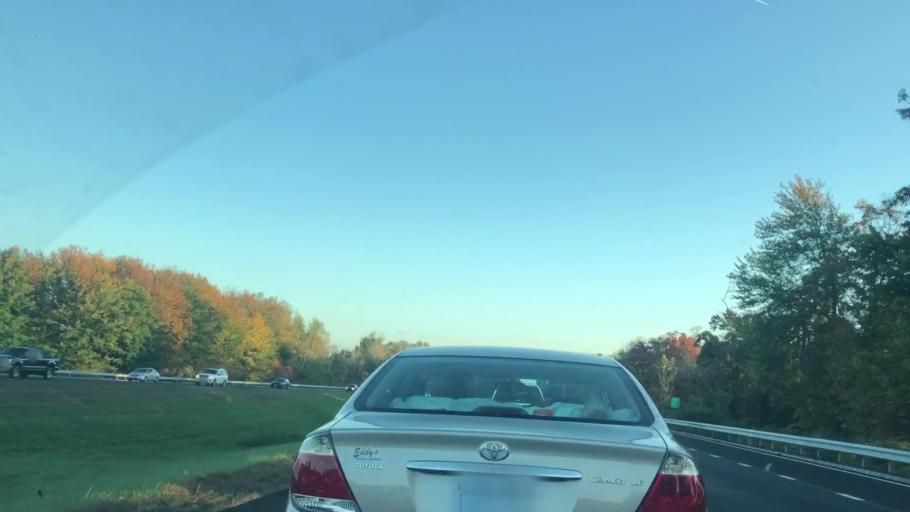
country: US
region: Massachusetts
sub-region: Franklin County
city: South Deerfield
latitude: 42.5033
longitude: -72.6198
